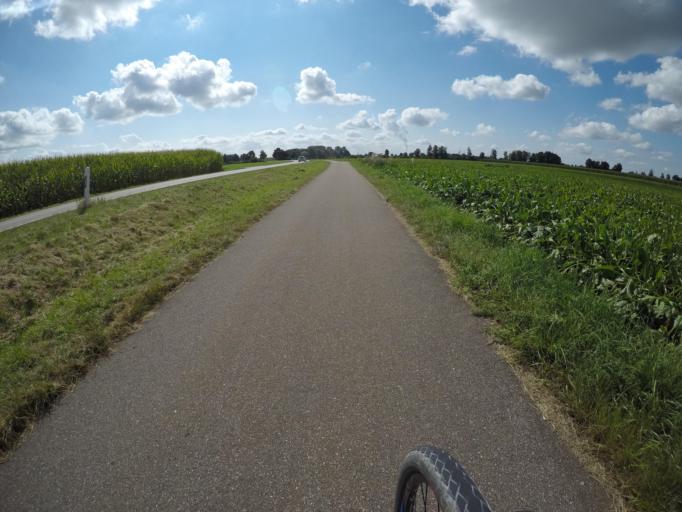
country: DE
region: Bavaria
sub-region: Swabia
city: Finningen
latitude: 48.6180
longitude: 10.5039
